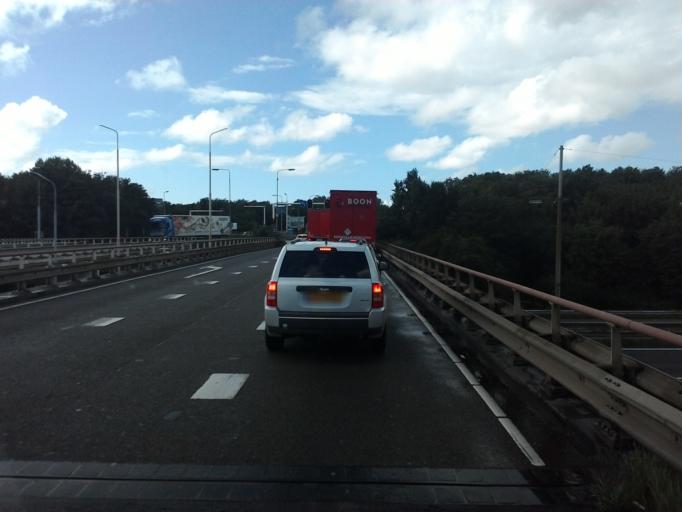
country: NL
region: North Holland
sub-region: Gemeente Beverwijk
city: Beverwijk
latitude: 52.4736
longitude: 4.6542
